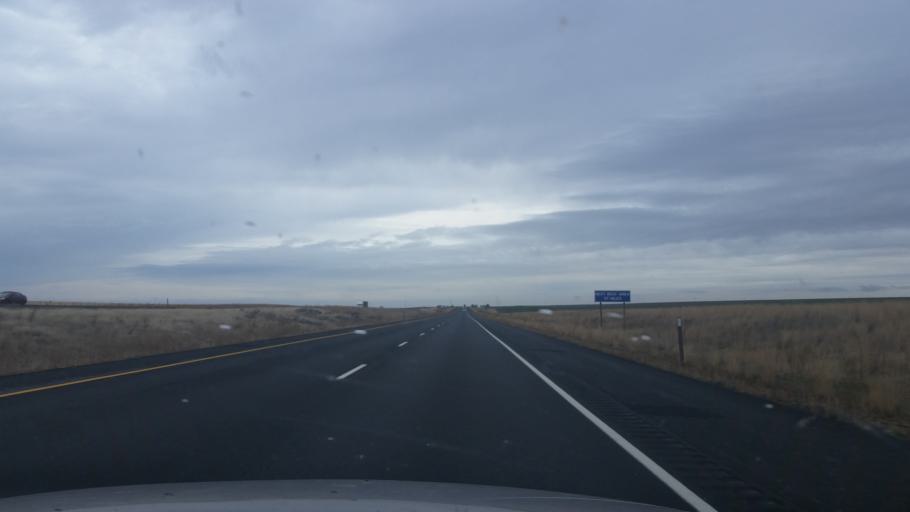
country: US
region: Washington
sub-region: Grant County
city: Warden
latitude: 47.0864
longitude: -118.7924
